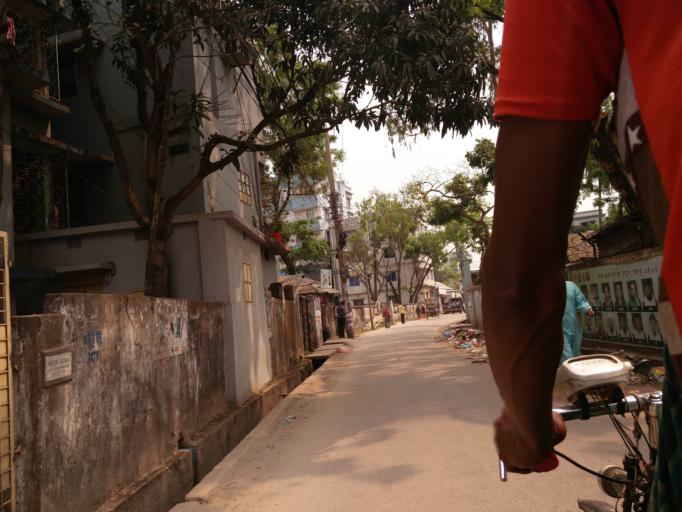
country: BD
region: Dhaka
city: Mymensingh
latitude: 24.7513
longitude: 90.4029
